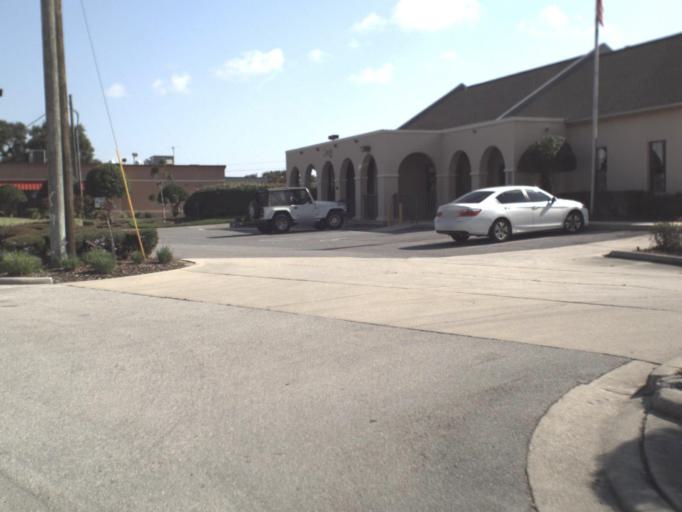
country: US
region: Florida
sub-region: Saint Johns County
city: Saint Augustine Beach
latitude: 29.8575
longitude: -81.2810
